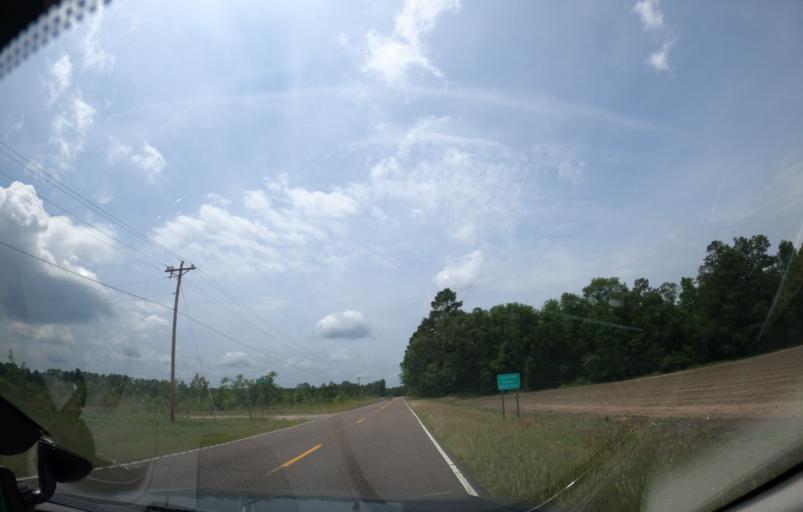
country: US
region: South Carolina
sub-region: Barnwell County
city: Williston
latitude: 33.5738
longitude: -81.4633
